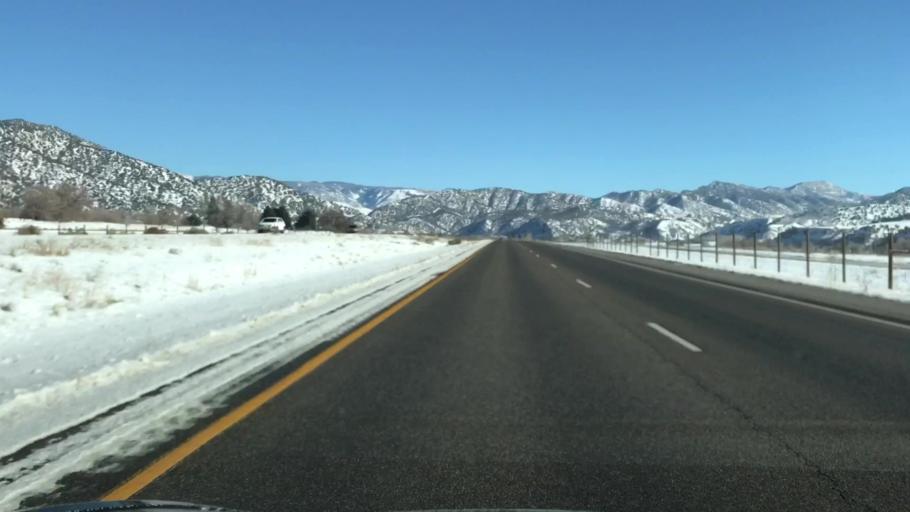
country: US
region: Colorado
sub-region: Garfield County
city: New Castle
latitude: 39.5532
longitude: -107.5835
